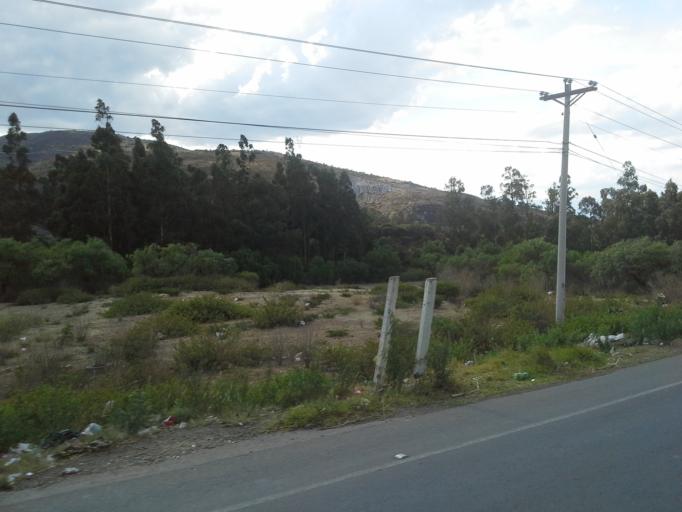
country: BO
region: Cochabamba
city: Tarata
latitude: -17.5049
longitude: -66.0890
